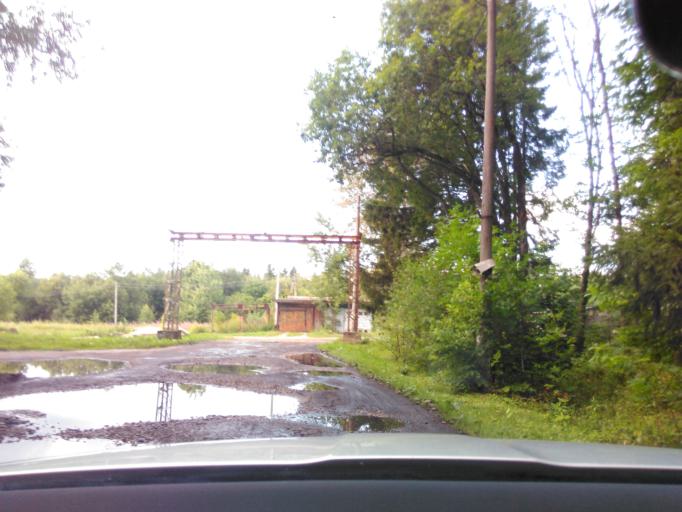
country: RU
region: Moskovskaya
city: Radumlya
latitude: 56.1310
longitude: 37.2117
